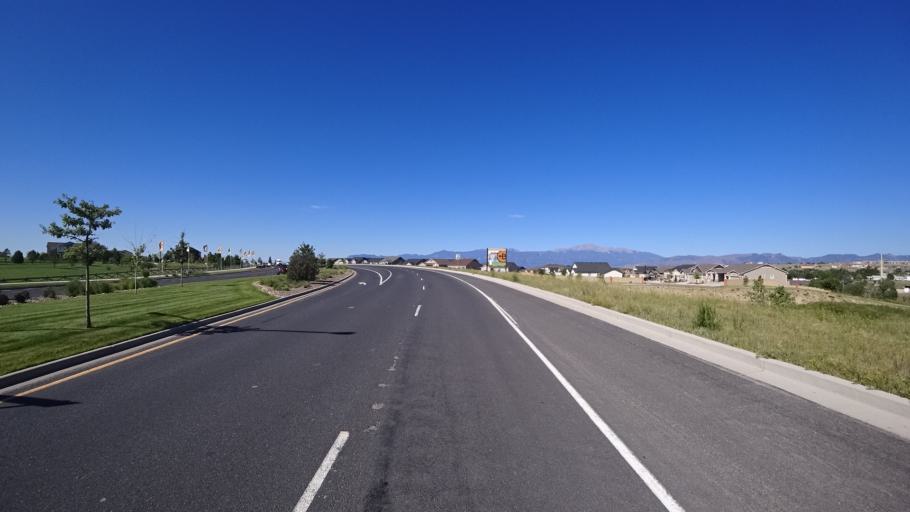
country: US
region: Colorado
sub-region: El Paso County
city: Cimarron Hills
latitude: 38.9360
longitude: -104.6816
